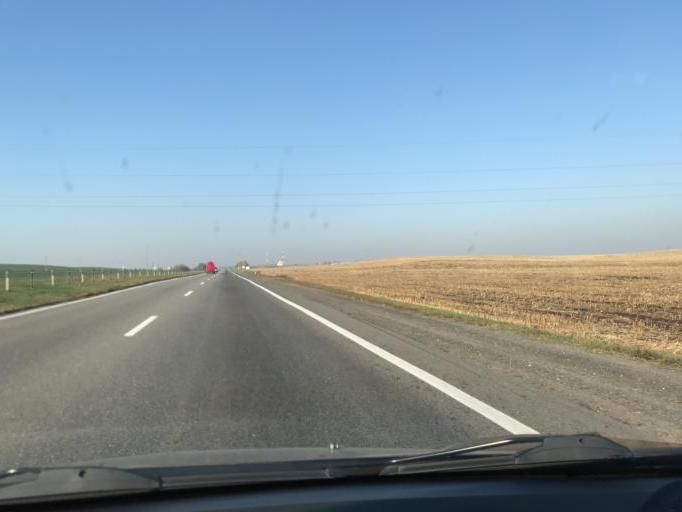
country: BY
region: Minsk
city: Luhavaya Slabada
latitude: 53.7211
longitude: 27.8625
